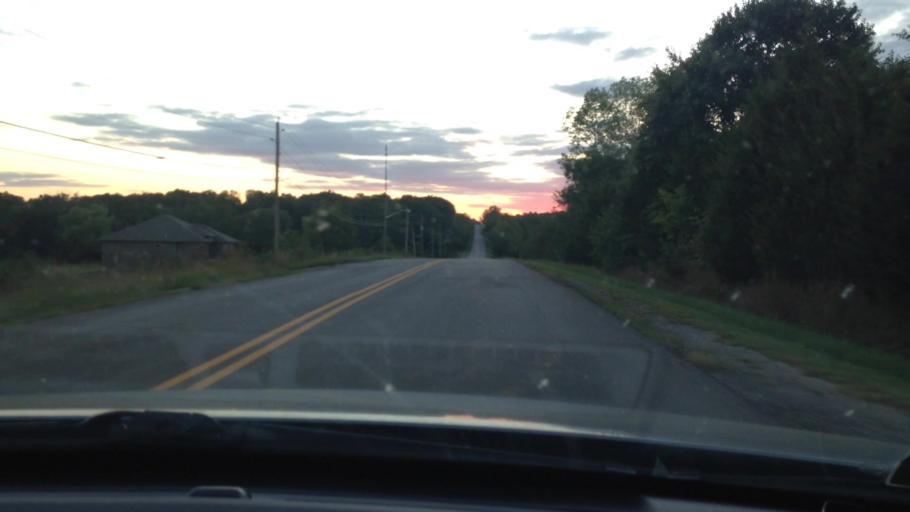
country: US
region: Kansas
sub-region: Leavenworth County
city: Lansing
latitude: 39.1871
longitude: -94.8693
